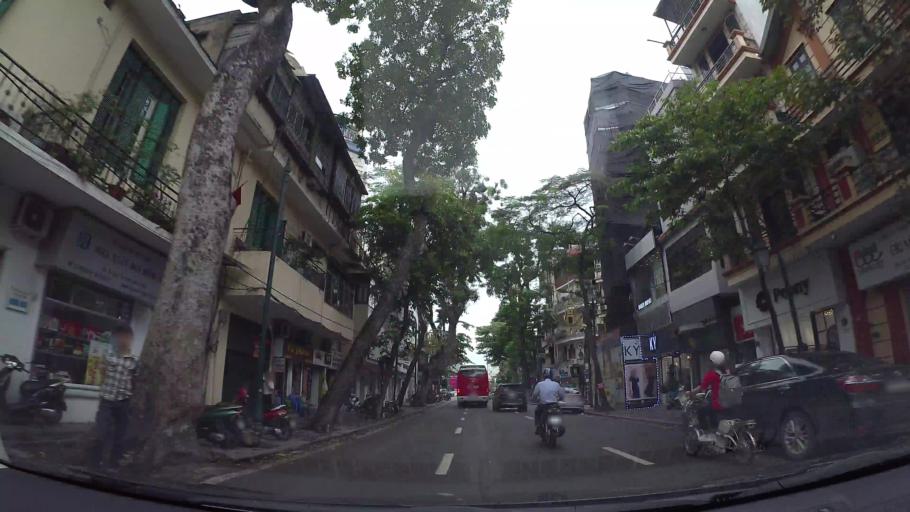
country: VN
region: Ha Noi
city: Hanoi
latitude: 21.0278
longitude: 105.8451
